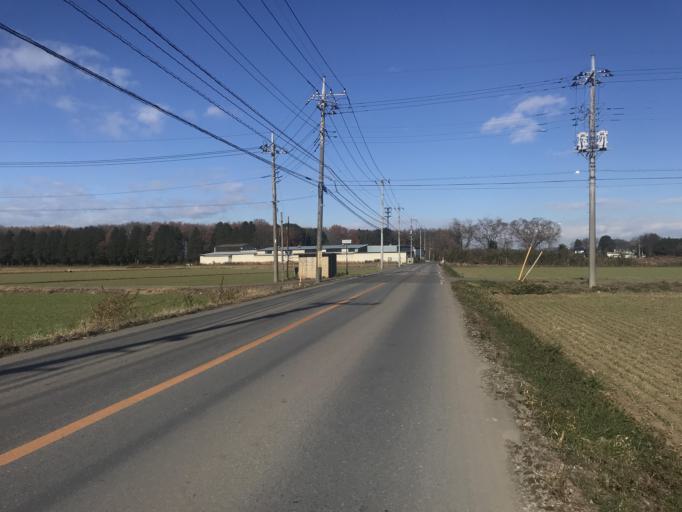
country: JP
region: Ibaraki
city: Yuki
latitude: 36.3534
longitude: 139.8774
